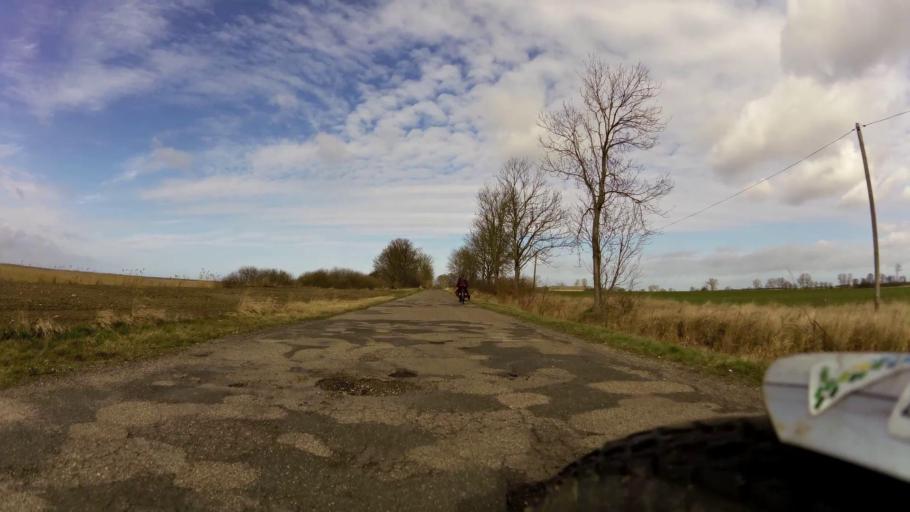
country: PL
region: West Pomeranian Voivodeship
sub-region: Powiat kamienski
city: Kamien Pomorski
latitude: 53.9859
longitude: 14.7692
